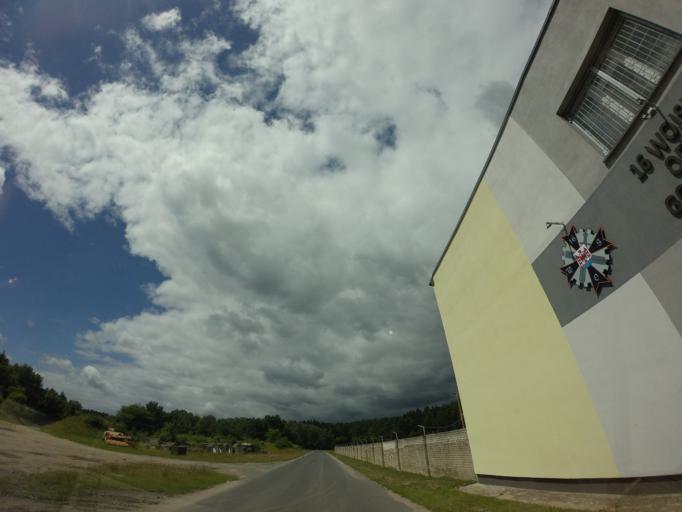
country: PL
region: West Pomeranian Voivodeship
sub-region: Powiat drawski
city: Drawsko Pomorskie
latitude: 53.4722
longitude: 15.7615
